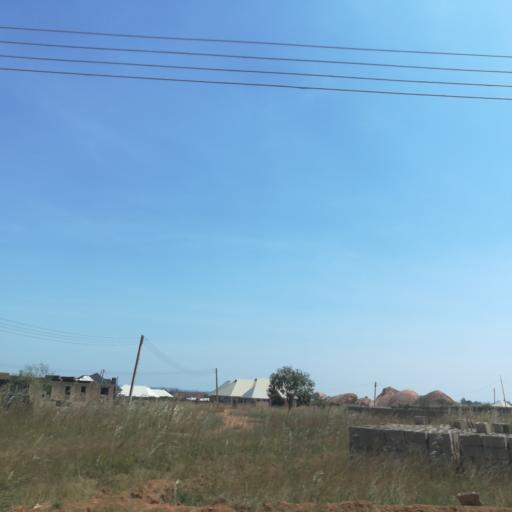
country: NG
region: Plateau
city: Bukuru
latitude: 9.8504
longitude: 8.9270
